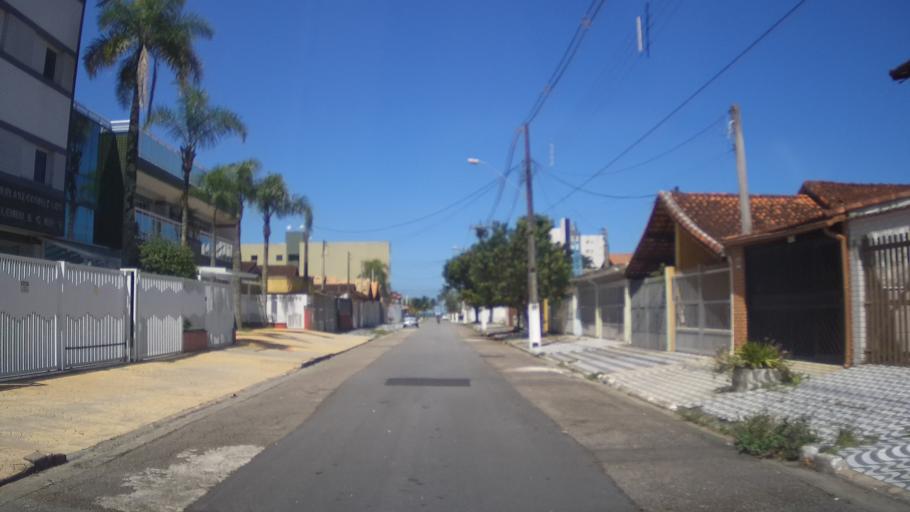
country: BR
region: Sao Paulo
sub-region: Mongagua
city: Mongagua
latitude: -24.0838
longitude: -46.6013
